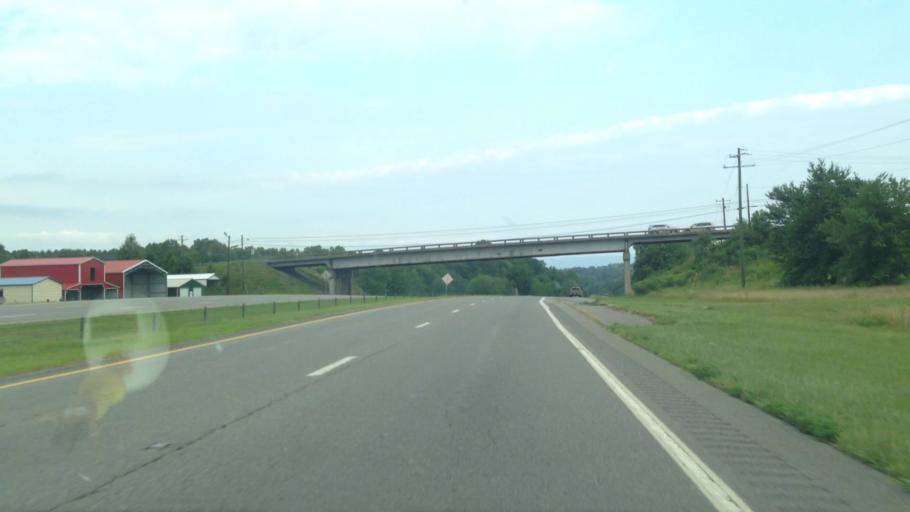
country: US
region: North Carolina
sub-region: Surry County
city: Flat Rock
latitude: 36.4593
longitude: -80.5602
